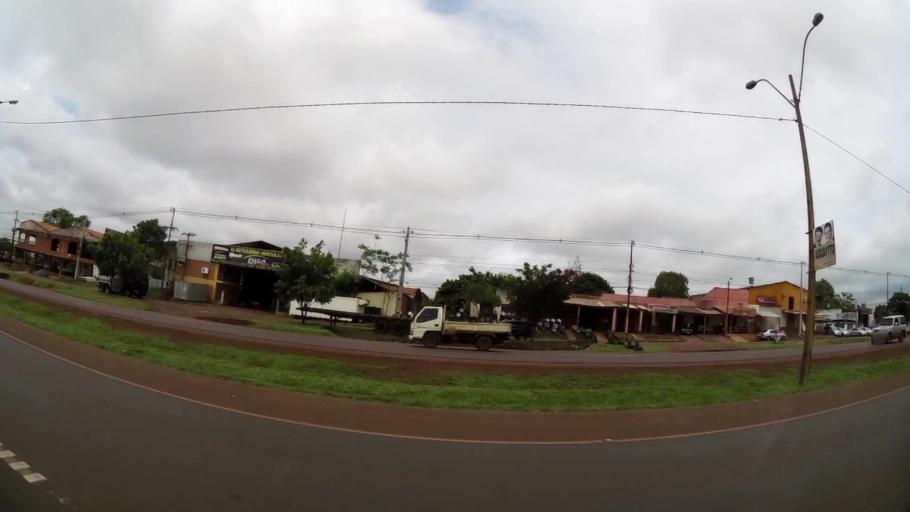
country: PY
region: Alto Parana
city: Ciudad del Este
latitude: -25.4944
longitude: -54.7051
